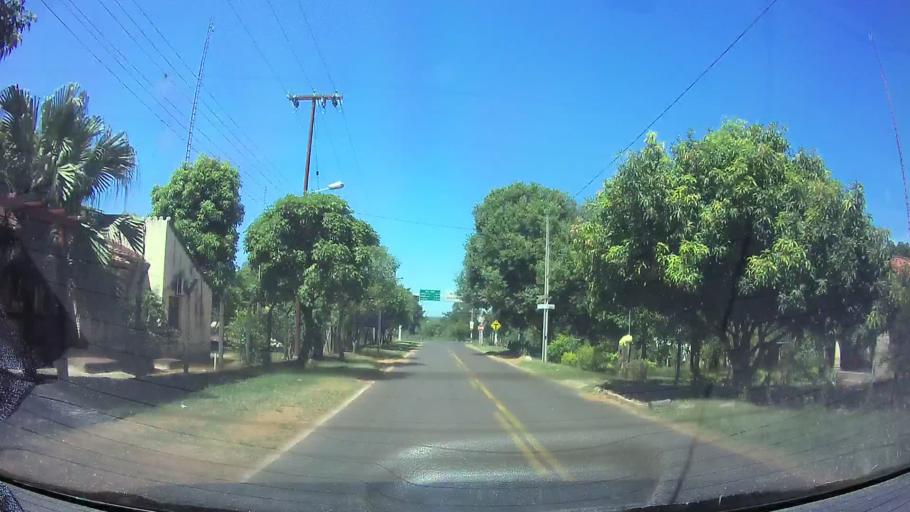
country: PY
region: Central
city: Aregua
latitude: -25.2828
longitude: -57.3990
